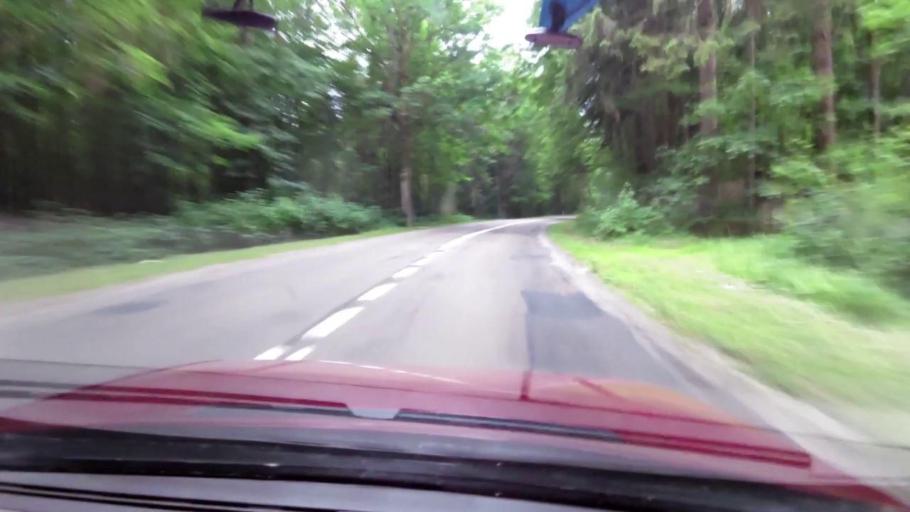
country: PL
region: West Pomeranian Voivodeship
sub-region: Powiat koszalinski
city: Sianow
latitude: 54.1885
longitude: 16.2812
